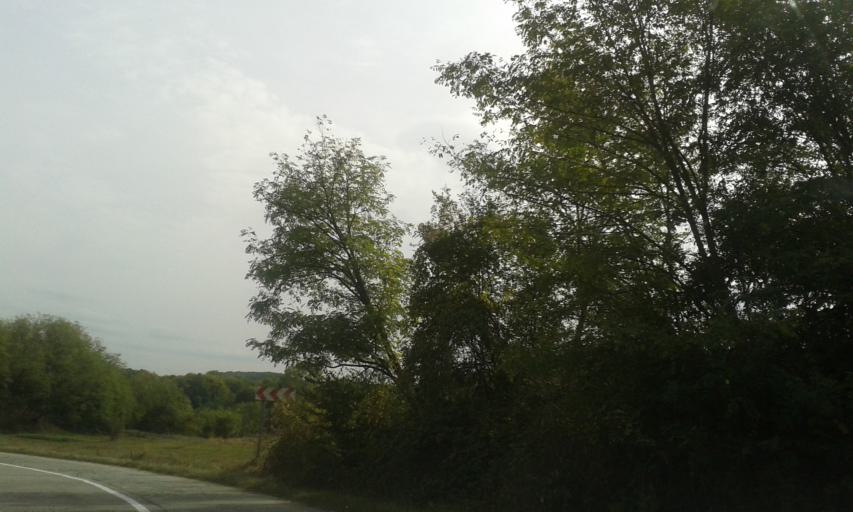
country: RO
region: Gorj
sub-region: Comuna Stejari
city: Piscoiu
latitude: 44.9124
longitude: 23.7694
